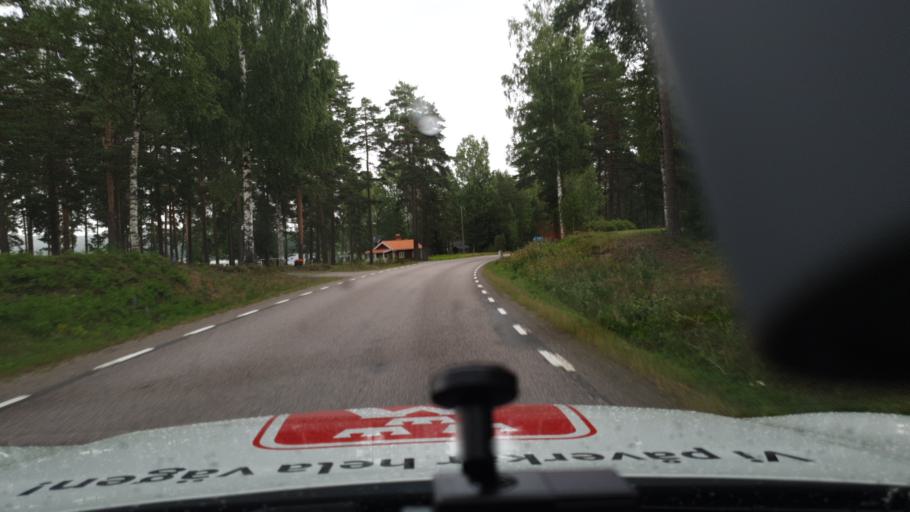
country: SE
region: Vaermland
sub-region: Torsby Kommun
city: Torsby
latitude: 59.9953
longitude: 12.8824
